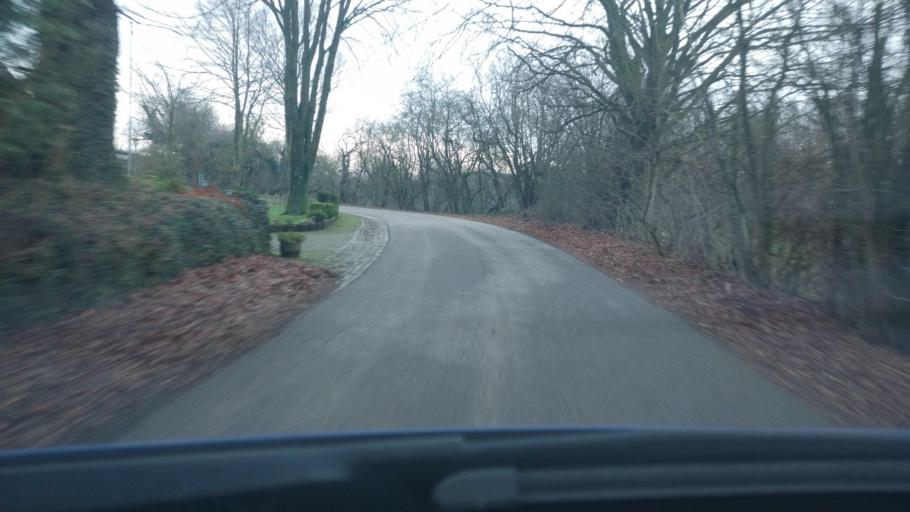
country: DE
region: Schleswig-Holstein
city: Neuberend
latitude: 54.5413
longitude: 9.5451
